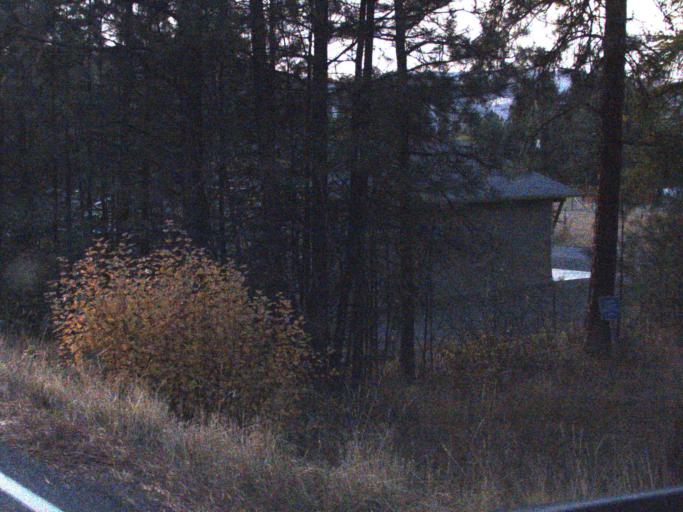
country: US
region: Washington
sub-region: Stevens County
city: Kettle Falls
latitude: 48.6649
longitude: -118.0555
